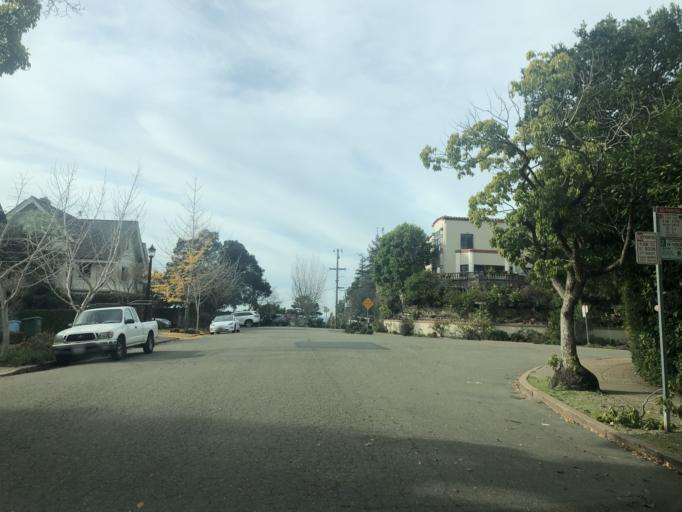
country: US
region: California
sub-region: Alameda County
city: Berkeley
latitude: 37.8598
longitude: -122.2468
